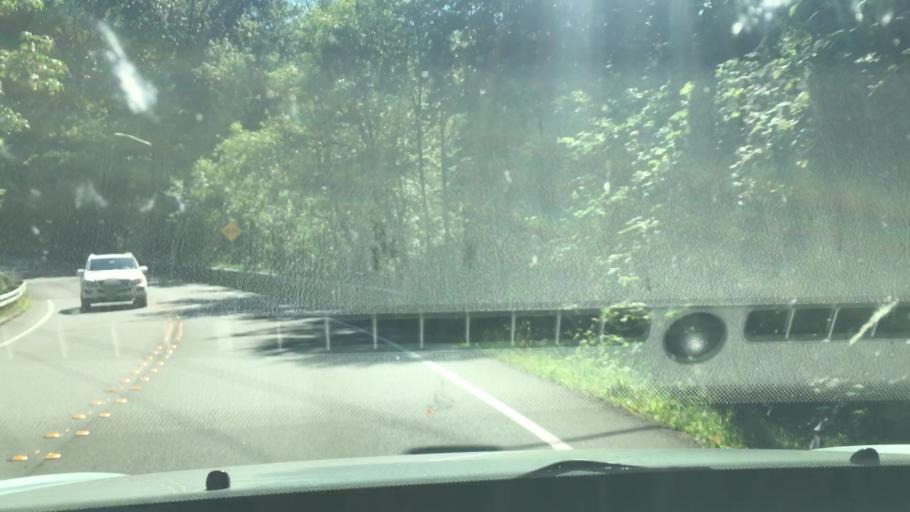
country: US
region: Washington
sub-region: King County
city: Newcastle
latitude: 47.5349
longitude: -122.1304
